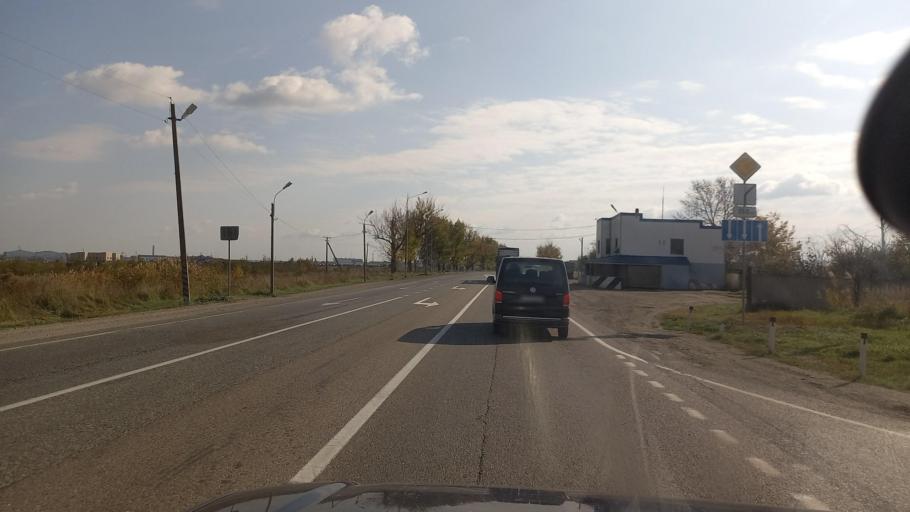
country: RU
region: Krasnodarskiy
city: Abinsk
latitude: 44.8722
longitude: 38.1232
